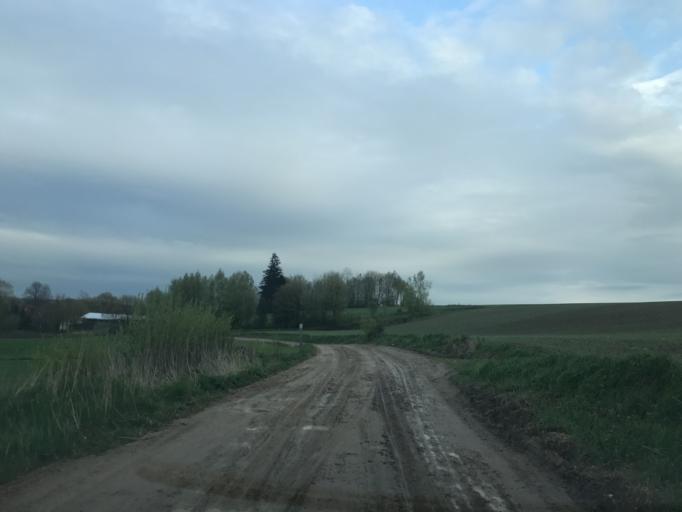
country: PL
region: Warmian-Masurian Voivodeship
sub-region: Powiat ilawski
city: Lubawa
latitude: 53.5338
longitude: 19.8952
